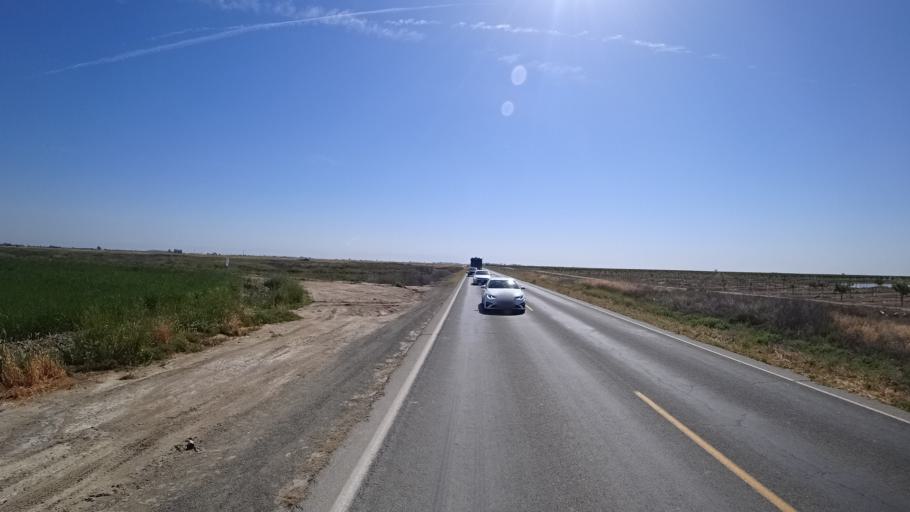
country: US
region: California
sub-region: Kings County
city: Stratford
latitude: 36.2111
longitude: -119.7398
